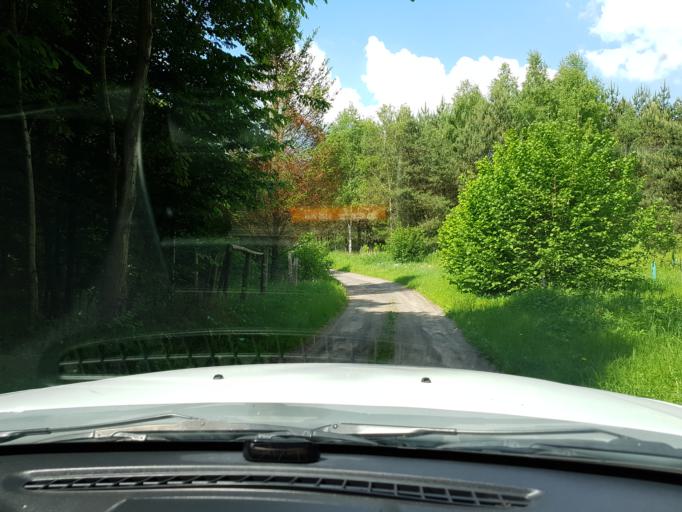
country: PL
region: West Pomeranian Voivodeship
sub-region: Powiat drawski
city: Drawsko Pomorskie
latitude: 53.5474
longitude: 15.7137
